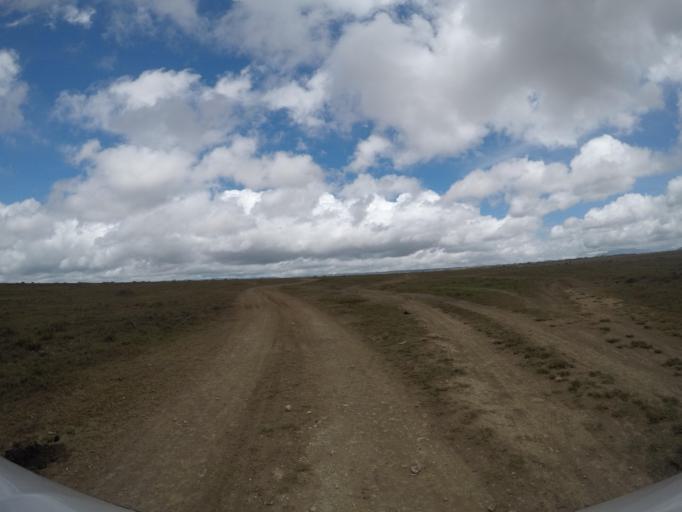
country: TL
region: Lautem
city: Lospalos
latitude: -8.4511
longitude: 126.9861
